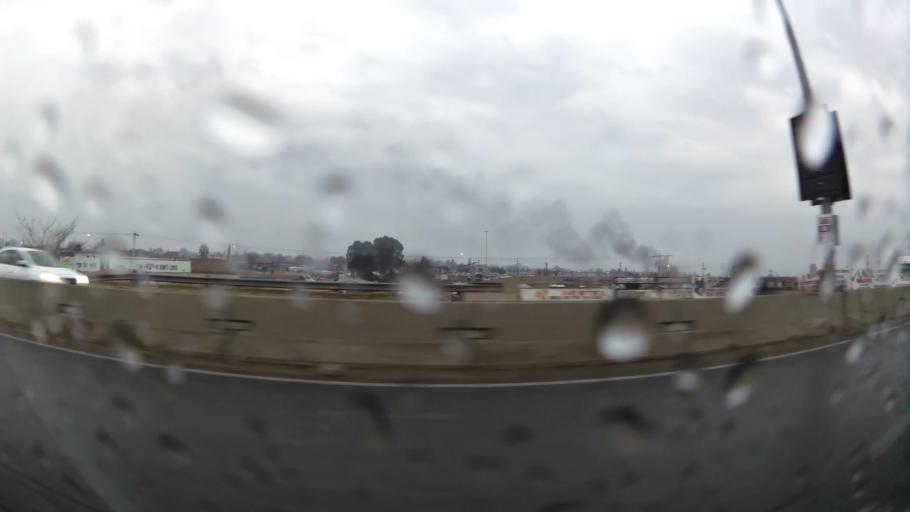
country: ZA
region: Gauteng
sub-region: City of Johannesburg Metropolitan Municipality
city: Soweto
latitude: -26.2613
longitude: 27.8975
